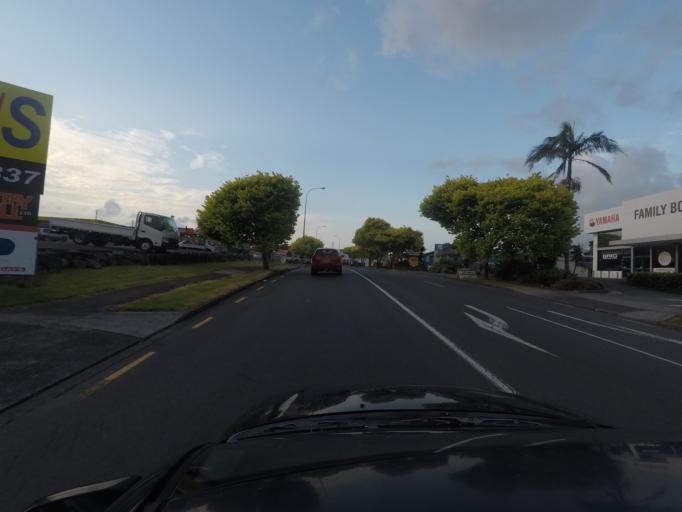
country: NZ
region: Auckland
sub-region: Auckland
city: Tamaki
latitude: -36.9263
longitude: 174.8917
